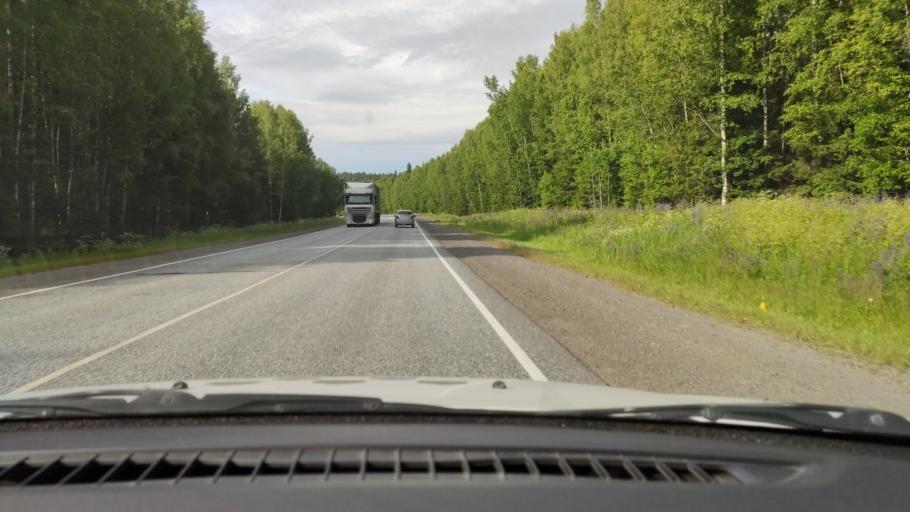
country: RU
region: Perm
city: Pavlovskiy
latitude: 57.9160
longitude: 54.9646
